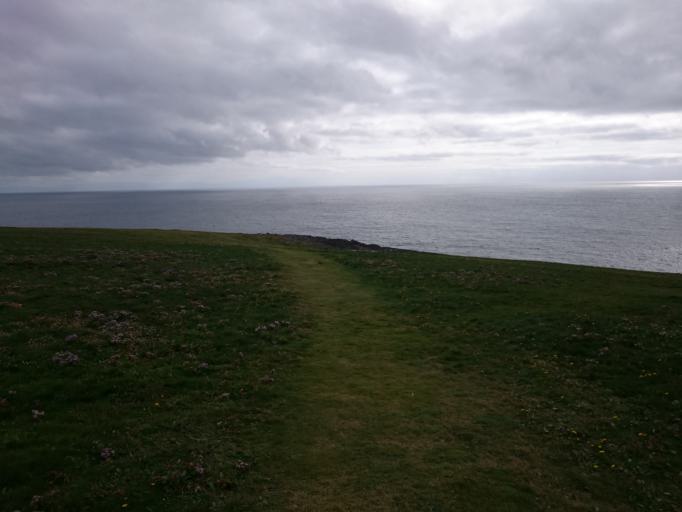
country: IE
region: Munster
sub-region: Ciarrai
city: Ballybunnion
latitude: 52.5598
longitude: -9.9375
